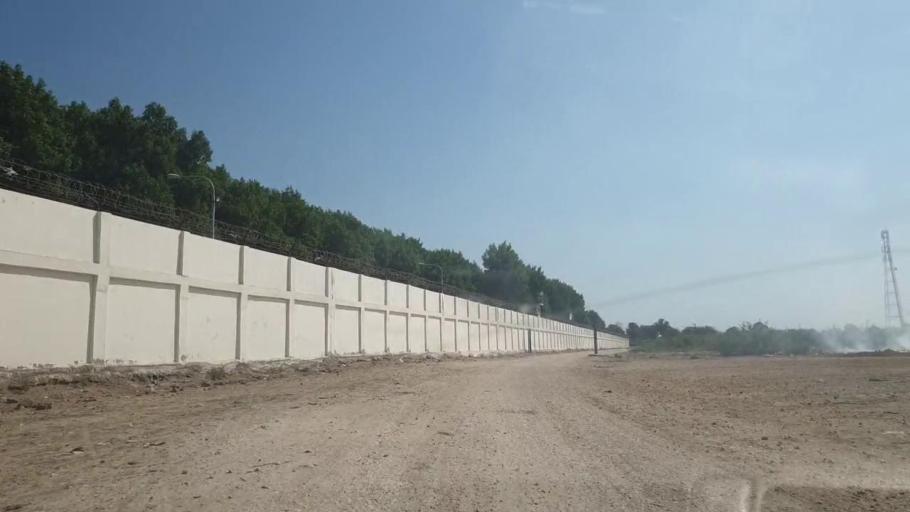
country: PK
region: Sindh
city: Tando Jam
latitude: 25.3819
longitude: 68.5799
